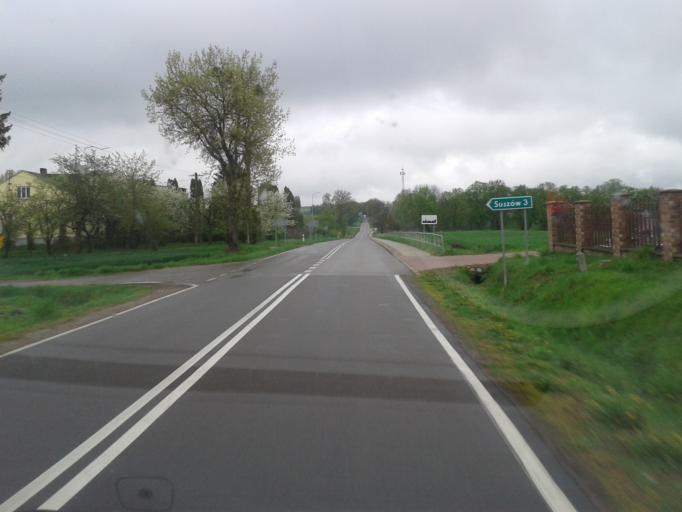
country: PL
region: Lublin Voivodeship
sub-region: Powiat tomaszowski
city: Telatyn
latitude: 50.5277
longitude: 23.9159
